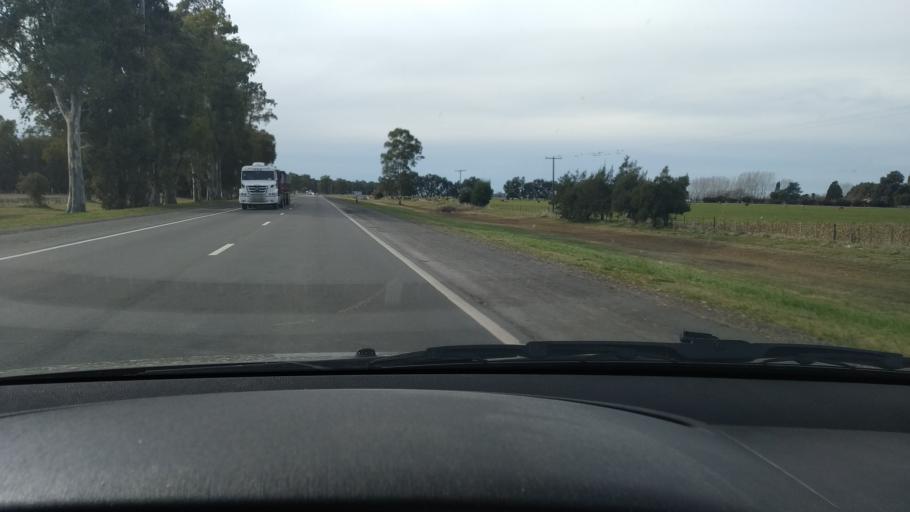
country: AR
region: Buenos Aires
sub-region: Partido de Azul
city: Azul
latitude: -36.7708
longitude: -59.8152
